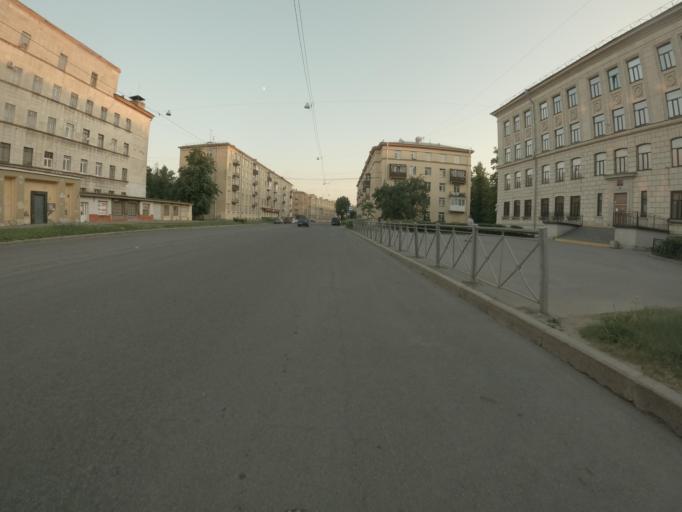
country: RU
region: St.-Petersburg
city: Avtovo
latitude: 59.8734
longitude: 30.2679
